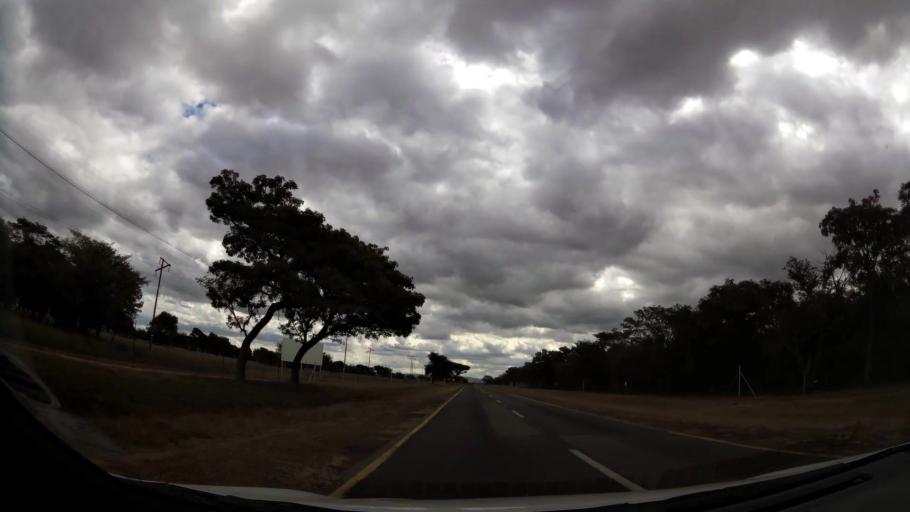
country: ZA
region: Limpopo
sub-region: Waterberg District Municipality
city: Modimolle
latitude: -24.7678
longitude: 28.4646
